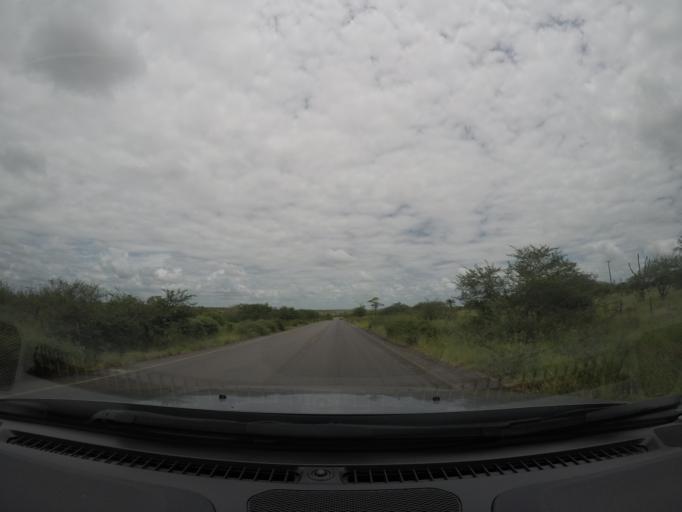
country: BR
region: Bahia
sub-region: Itaberaba
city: Itaberaba
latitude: -12.4914
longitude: -40.2340
